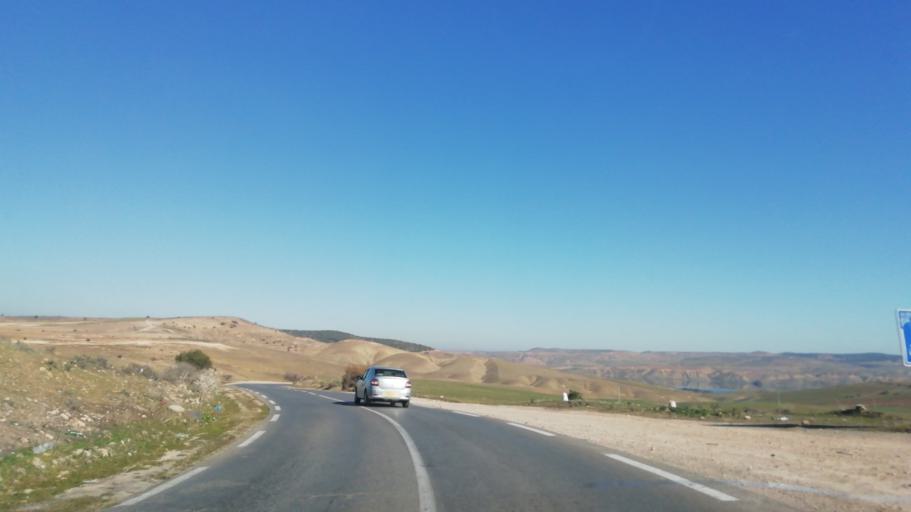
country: DZ
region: Tlemcen
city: Nedroma
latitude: 34.8304
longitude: -1.6733
